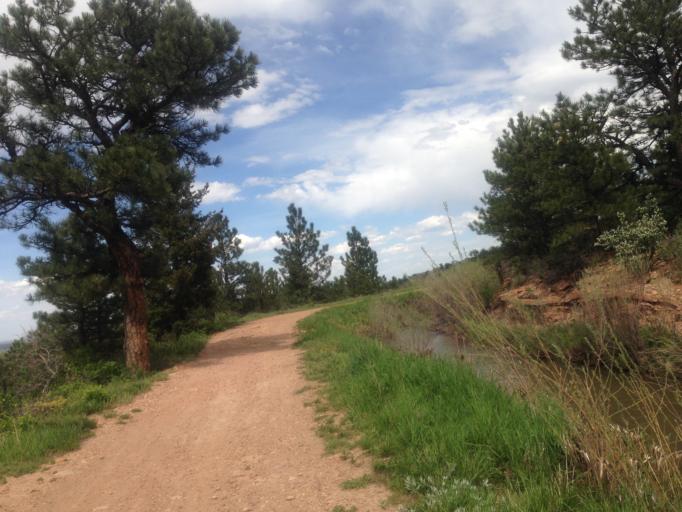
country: US
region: Colorado
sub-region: Boulder County
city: Superior
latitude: 39.9487
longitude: -105.2287
